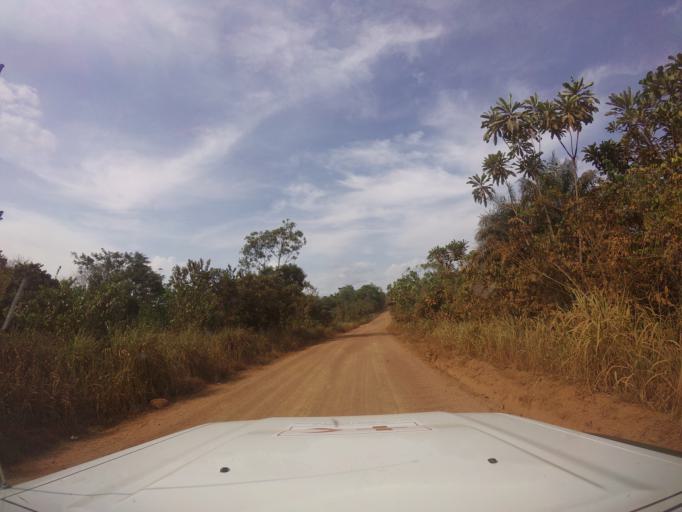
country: LR
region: Grand Cape Mount
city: Robertsport
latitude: 6.7131
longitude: -11.0860
